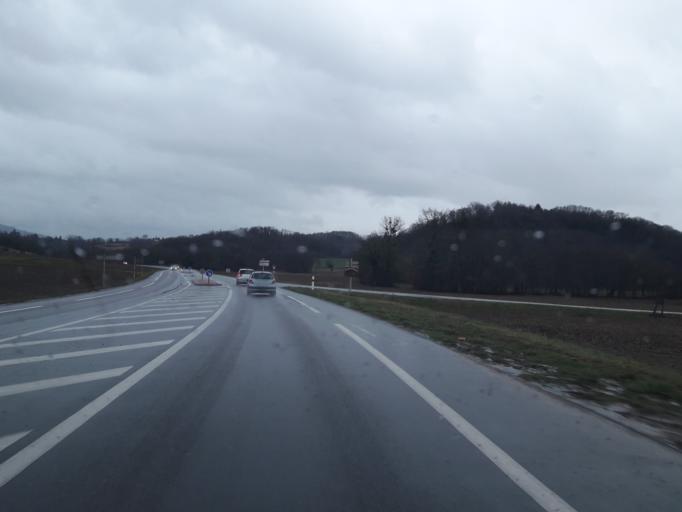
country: FR
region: Rhone-Alpes
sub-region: Departement de l'Ain
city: Belley
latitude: 45.7928
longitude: 5.6826
